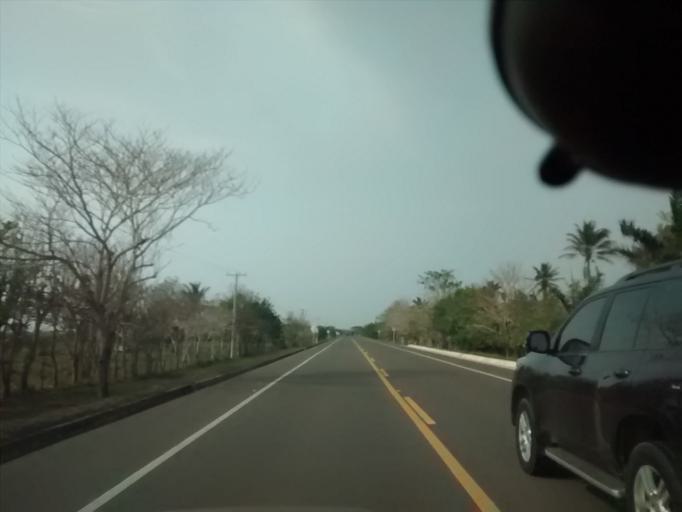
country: CO
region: Bolivar
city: Clemencia
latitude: 10.6442
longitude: -75.4019
